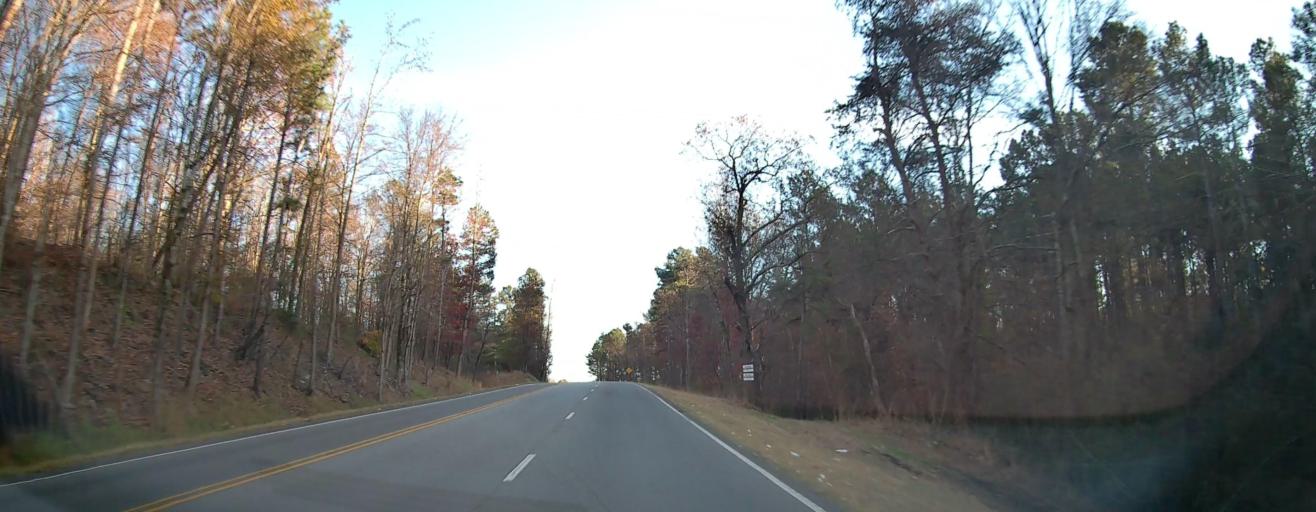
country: US
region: Alabama
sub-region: Blount County
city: Blountsville
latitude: 34.1475
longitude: -86.4517
